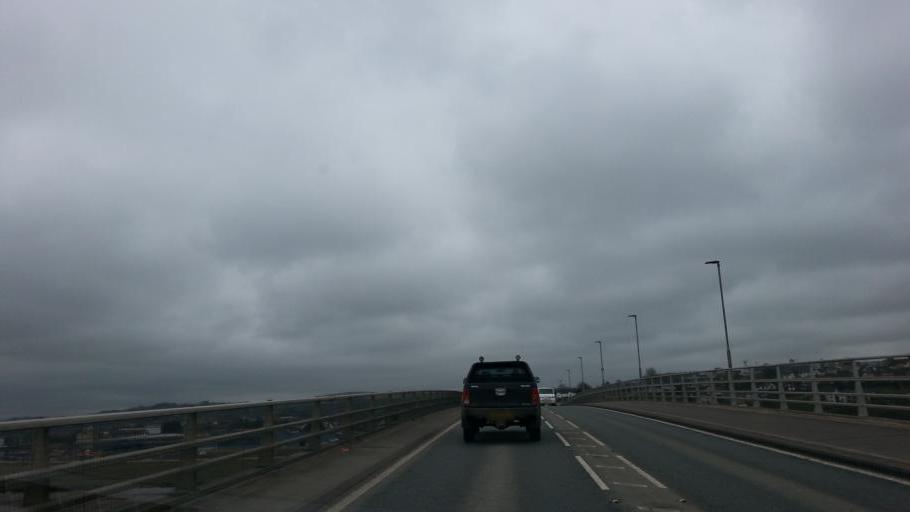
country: GB
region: England
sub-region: Devon
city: Barnstaple
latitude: 51.0804
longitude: -4.0714
